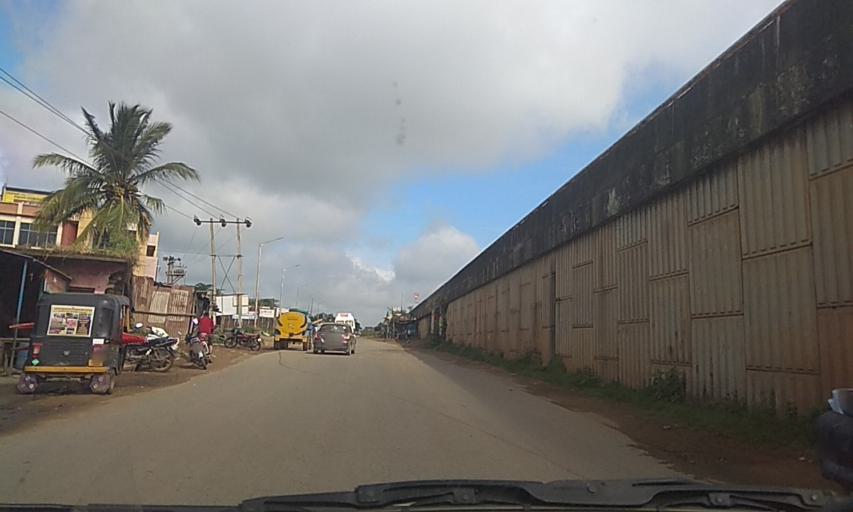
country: IN
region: Karnataka
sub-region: Haveri
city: Shiggaon
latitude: 14.9894
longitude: 75.2190
